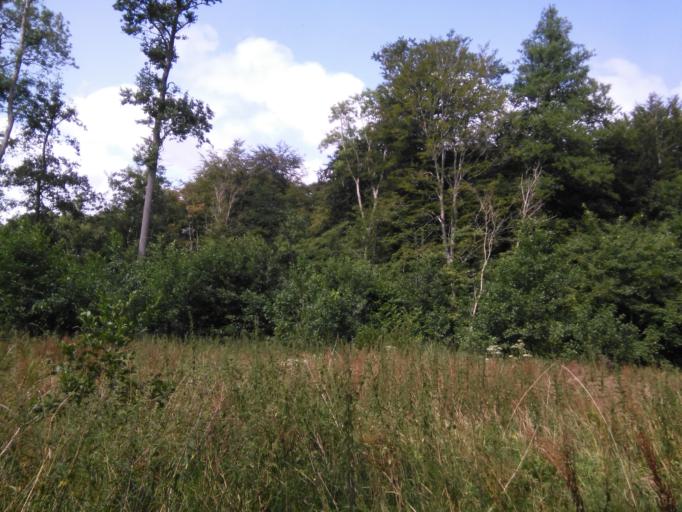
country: DK
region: Central Jutland
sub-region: Odder Kommune
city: Odder
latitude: 55.8831
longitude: 10.0394
